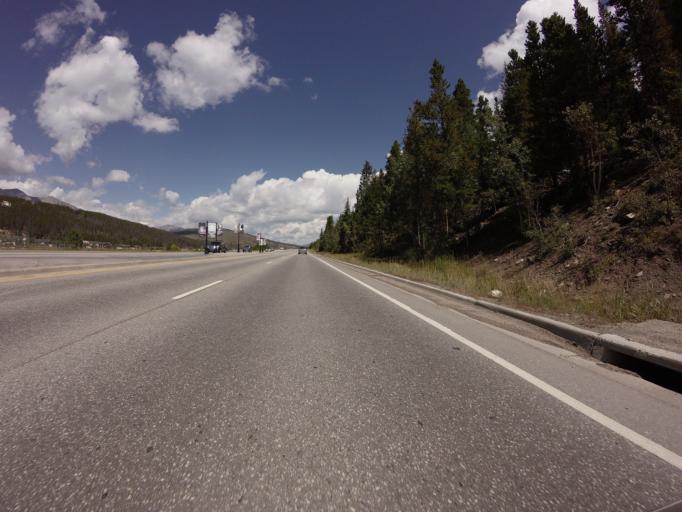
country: US
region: Colorado
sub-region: Summit County
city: Breckenridge
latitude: 39.5010
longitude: -106.0470
